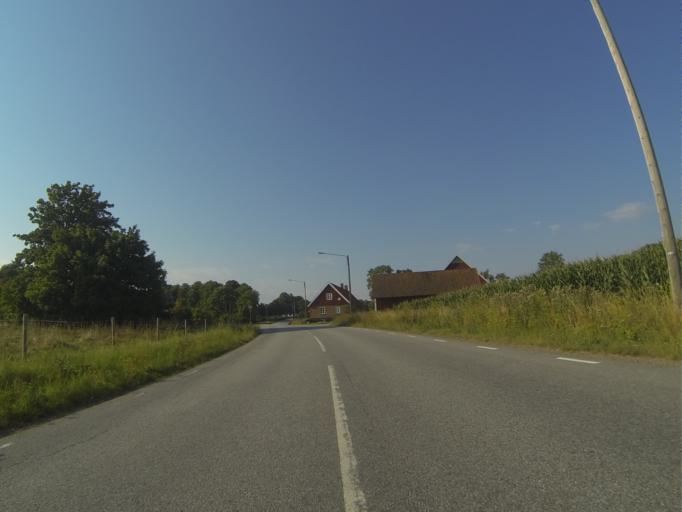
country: SE
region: Skane
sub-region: Lunds Kommun
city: Genarp
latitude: 55.6126
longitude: 13.4063
